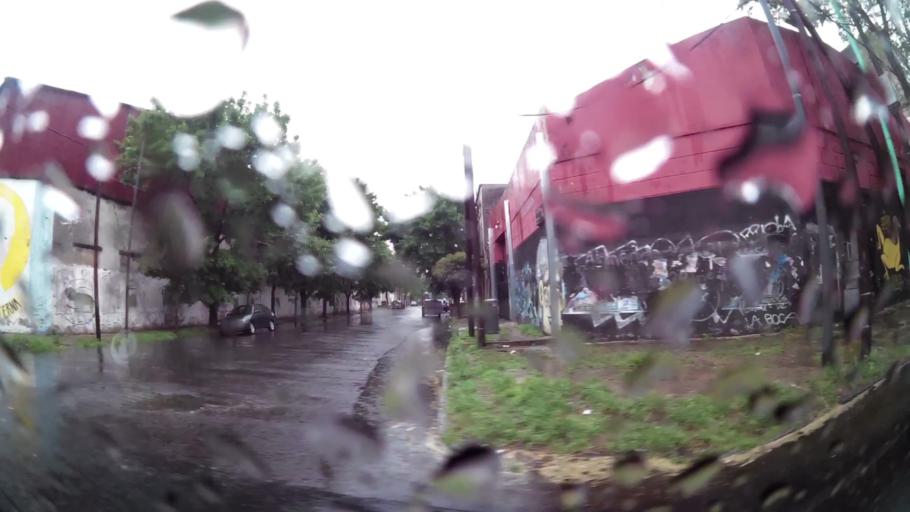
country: AR
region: Buenos Aires
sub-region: Partido de Avellaneda
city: Avellaneda
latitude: -34.6429
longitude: -58.3632
